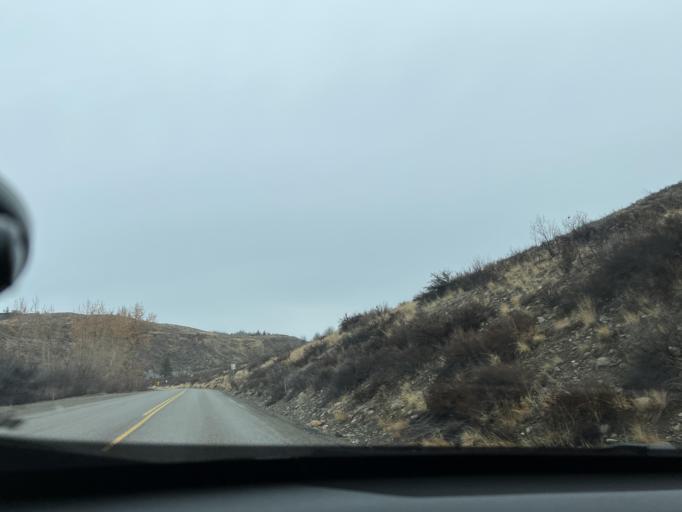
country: US
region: Washington
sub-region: Chelan County
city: Granite Falls
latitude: 48.4641
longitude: -120.2469
